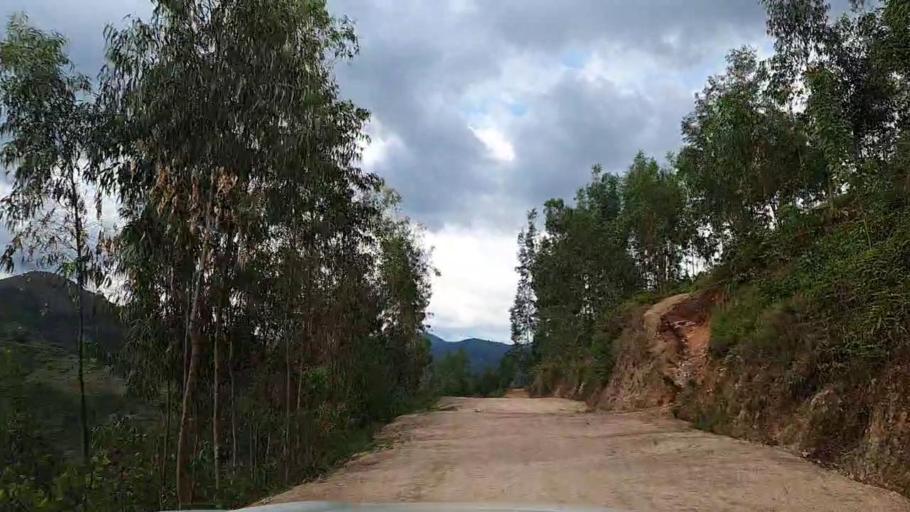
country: RW
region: Southern Province
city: Gikongoro
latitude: -2.4293
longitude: 29.6396
